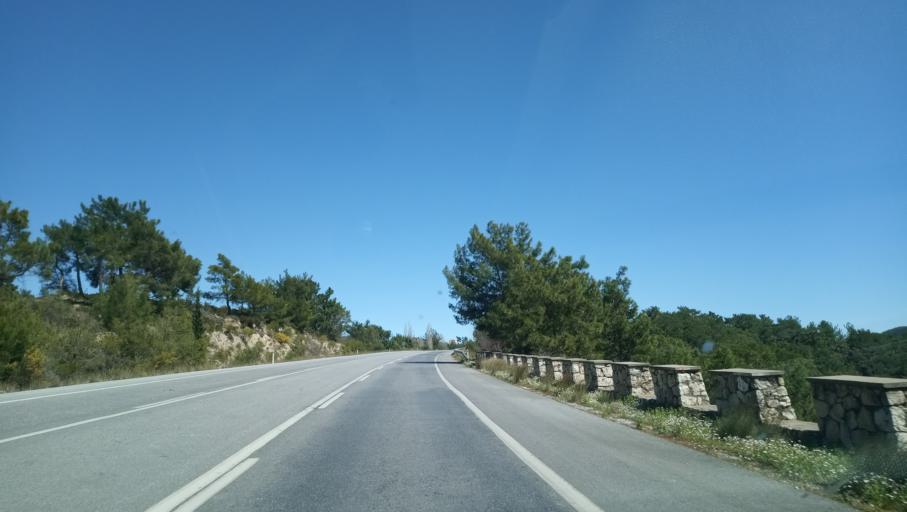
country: TR
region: Antalya
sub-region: Manavgat
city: Kizilagac
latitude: 36.7544
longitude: 31.6281
